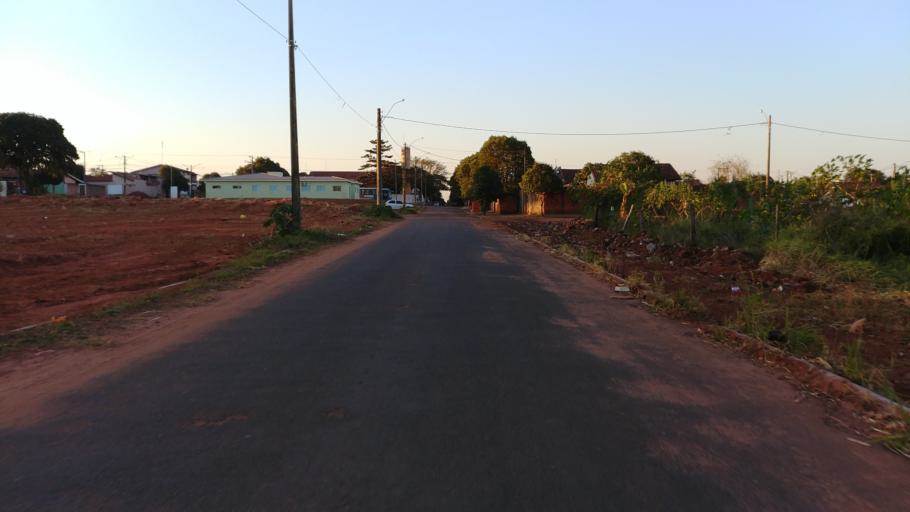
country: BR
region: Sao Paulo
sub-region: Paraguacu Paulista
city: Paraguacu Paulista
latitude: -22.4321
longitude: -50.5746
